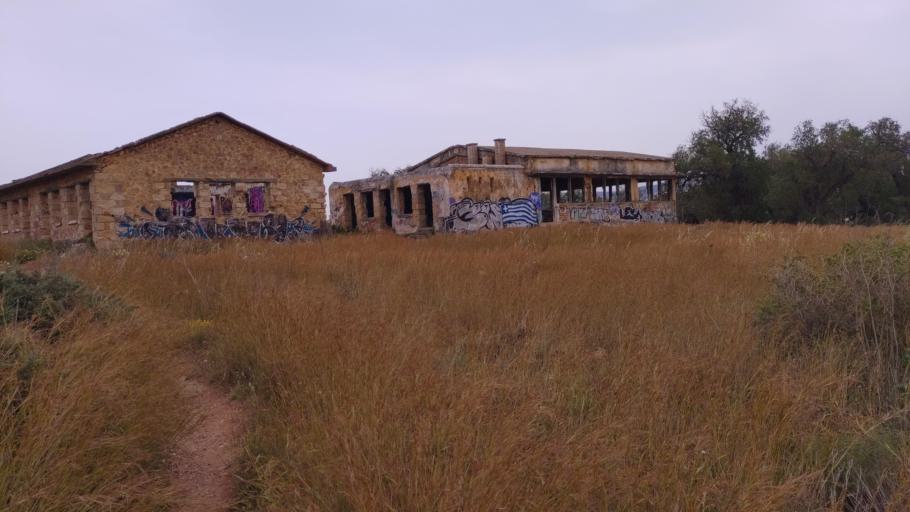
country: GR
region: Crete
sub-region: Nomos Chanias
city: Daratsos
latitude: 35.5149
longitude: 23.9803
